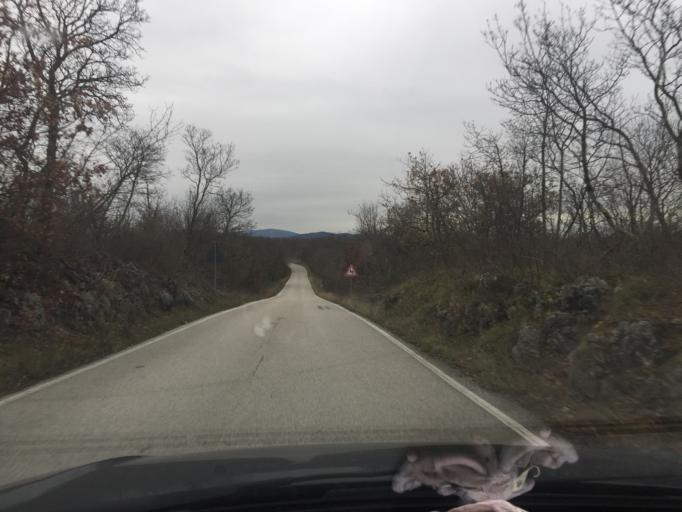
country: IT
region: Friuli Venezia Giulia
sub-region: Provincia di Trieste
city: Zolla
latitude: 45.7107
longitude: 13.8125
